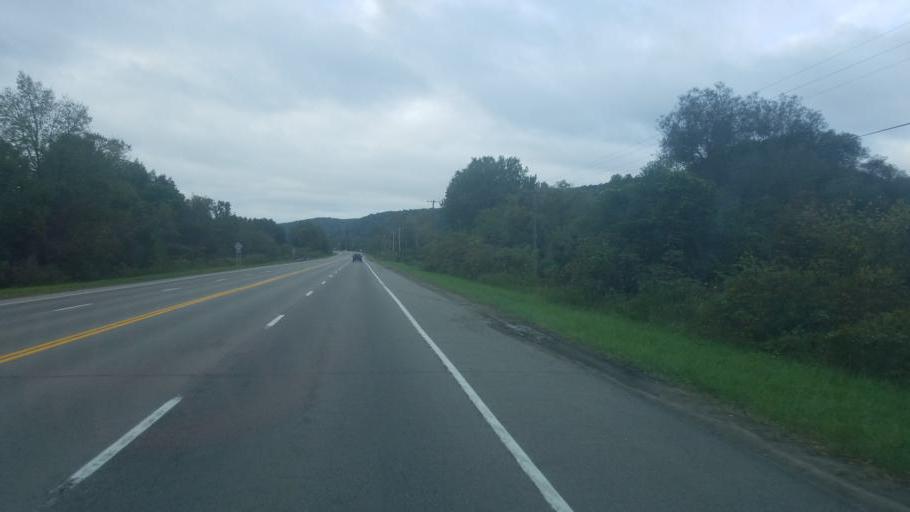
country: US
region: New York
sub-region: Cattaraugus County
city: Weston Mills
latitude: 42.1684
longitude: -78.3898
